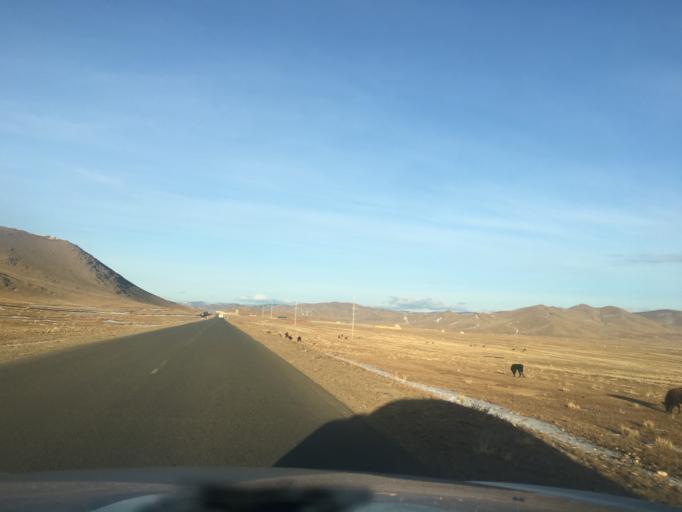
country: MN
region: Central Aimak
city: Mandal
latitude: 48.1140
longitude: 106.6409
